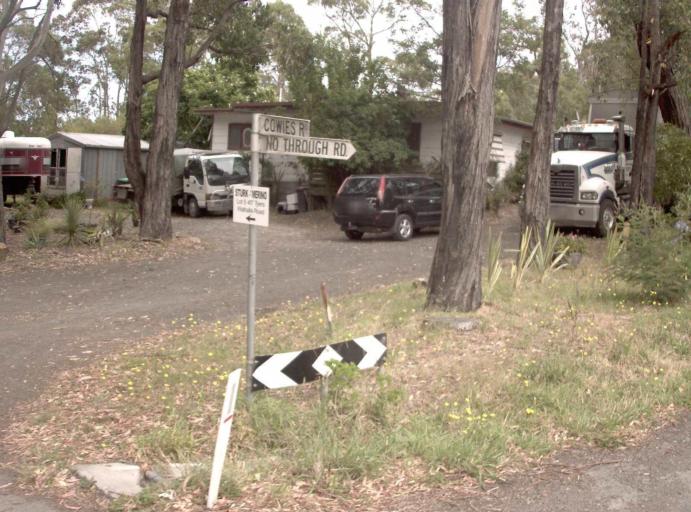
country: AU
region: Victoria
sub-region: Latrobe
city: Traralgon
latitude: -38.1271
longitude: 146.4711
